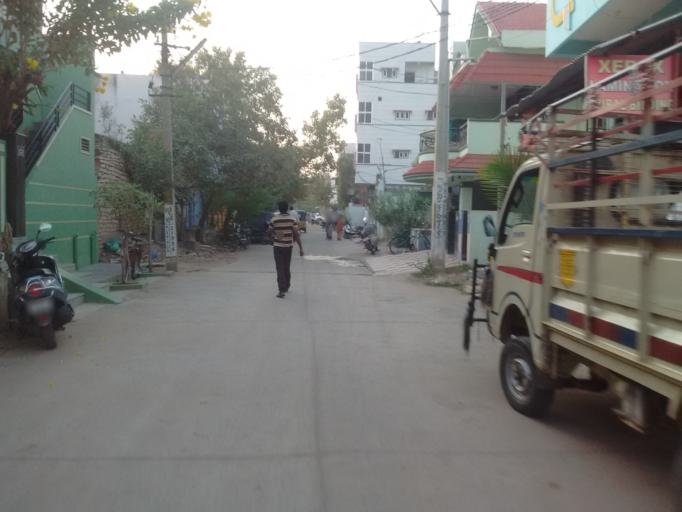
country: IN
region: Telangana
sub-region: Mahbubnagar
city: Alampur
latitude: 15.8116
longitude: 78.0432
